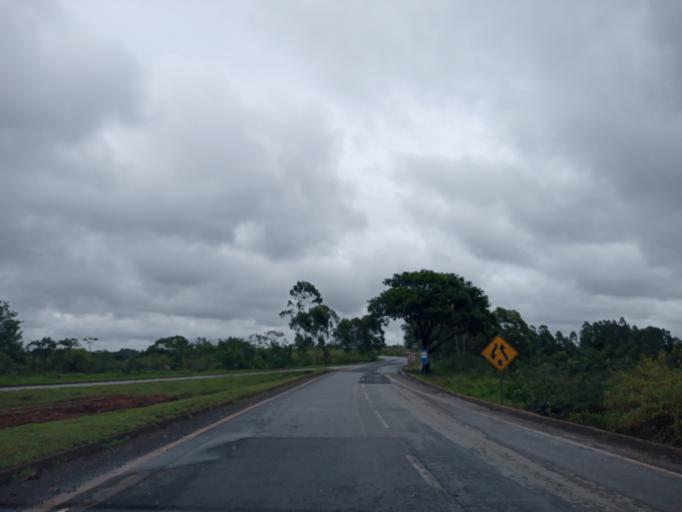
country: BR
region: Minas Gerais
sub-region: Campos Altos
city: Campos Altos
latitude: -19.6486
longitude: -46.0721
